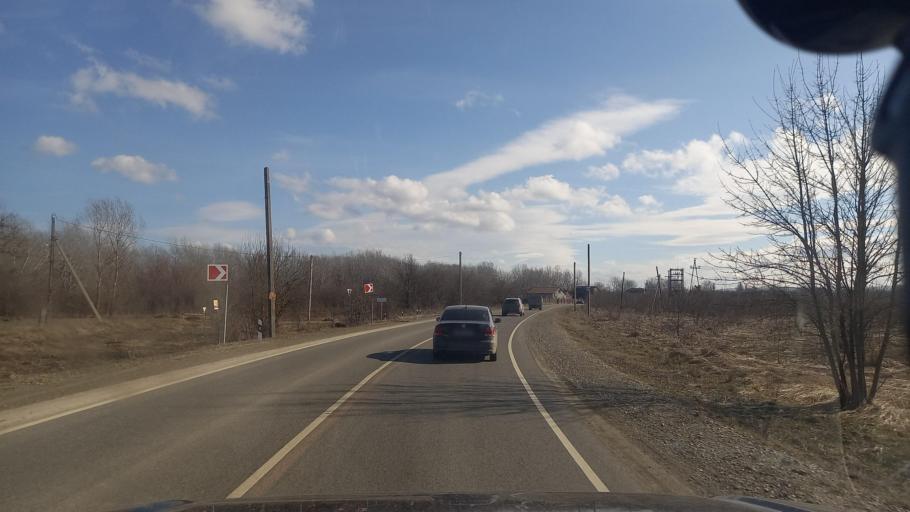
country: RU
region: Krasnodarskiy
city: Novodmitriyevskaya
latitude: 44.7820
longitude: 38.9716
